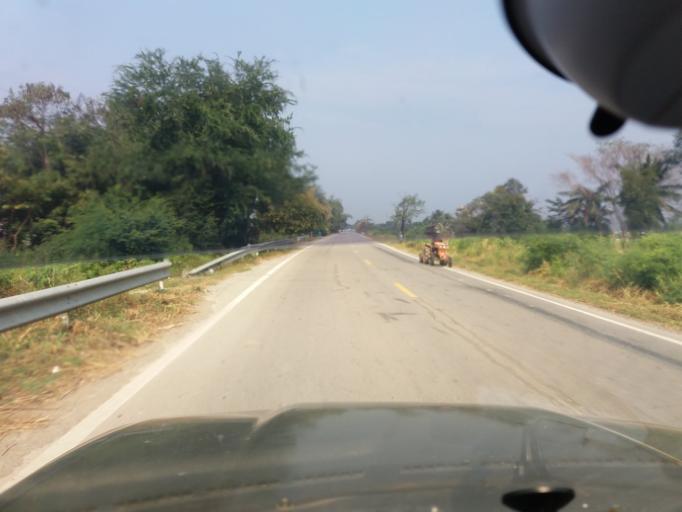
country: TH
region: Sing Buri
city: Bang Racham
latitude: 14.9106
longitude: 100.2579
